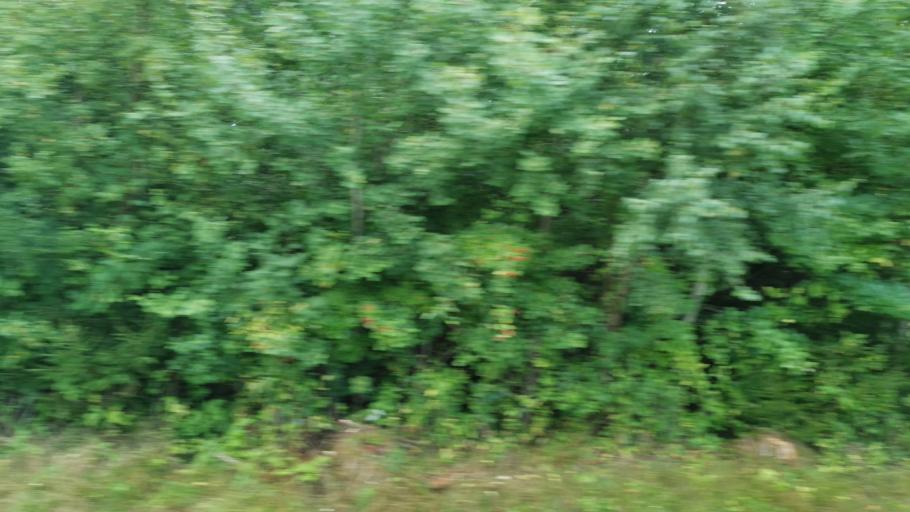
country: SE
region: Vaestra Goetaland
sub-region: Sotenas Kommun
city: Hunnebostrand
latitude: 58.5301
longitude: 11.2930
